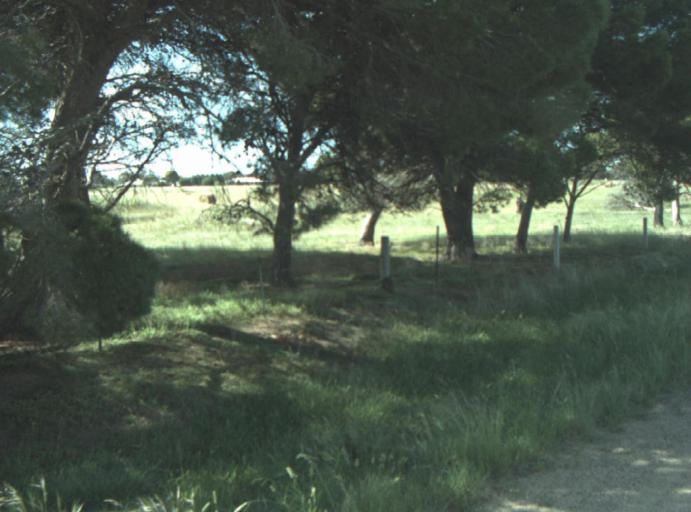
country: AU
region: Victoria
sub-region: Greater Geelong
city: Lara
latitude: -37.9935
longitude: 144.4204
